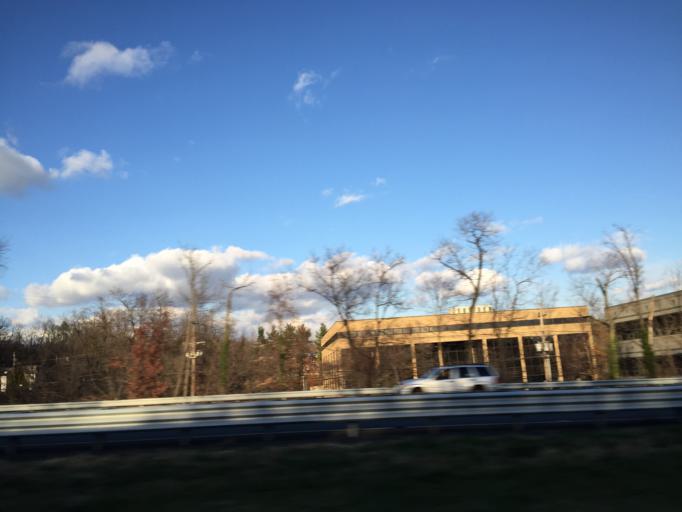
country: US
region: New Jersey
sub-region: Union County
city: Springfield
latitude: 40.7224
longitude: -74.3381
